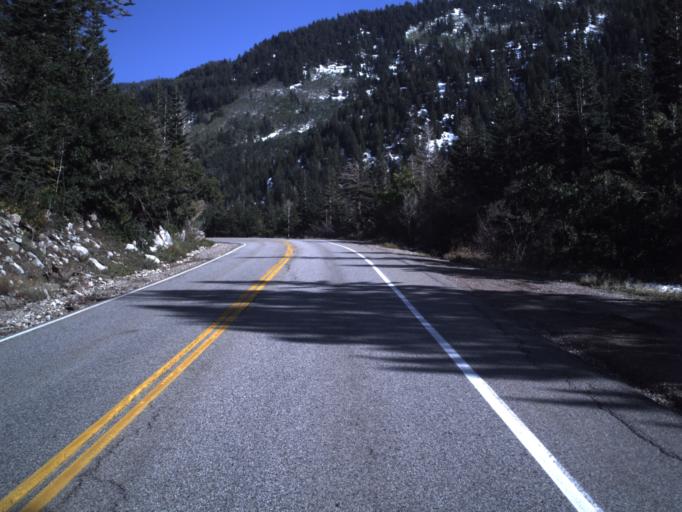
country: US
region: Utah
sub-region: Salt Lake County
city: Granite
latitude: 40.5709
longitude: -111.7107
